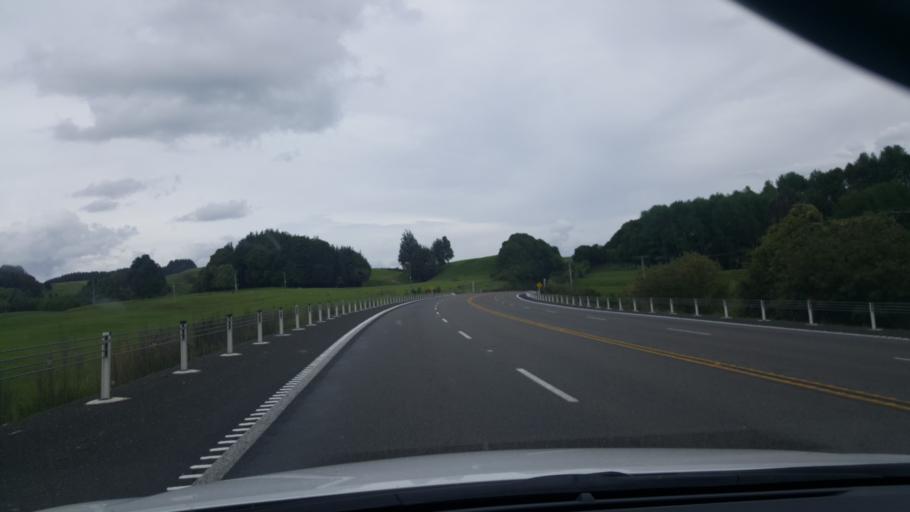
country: NZ
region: Bay of Plenty
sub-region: Rotorua District
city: Rotorua
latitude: -38.2481
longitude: 176.3161
